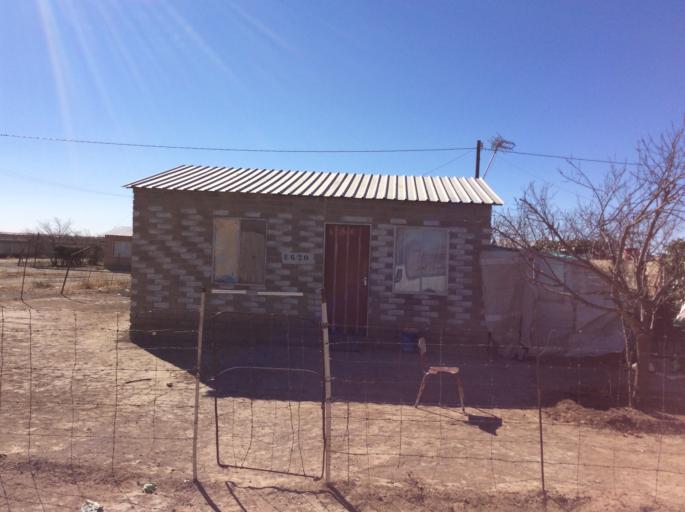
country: ZA
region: Orange Free State
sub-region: Lejweleputswa District Municipality
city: Brandfort
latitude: -28.7341
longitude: 26.1048
